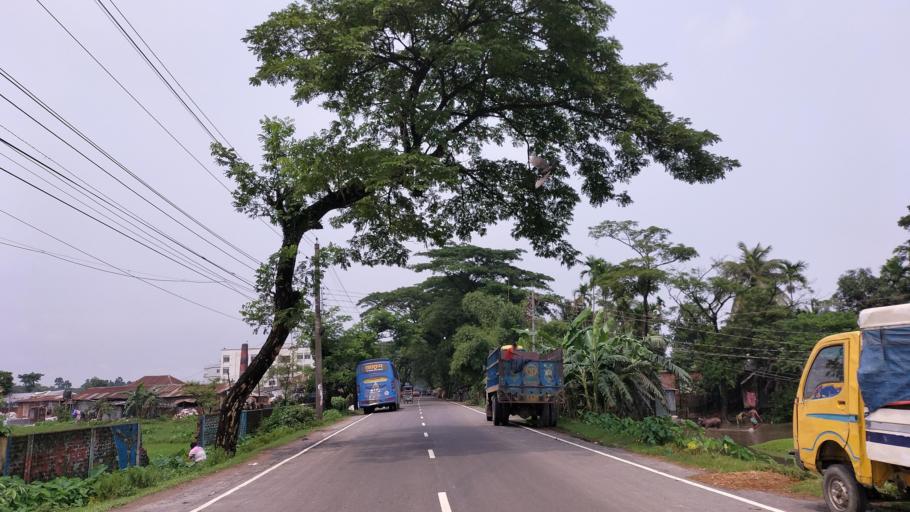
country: BD
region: Dhaka
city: Netrakona
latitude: 24.8959
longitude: 90.7442
